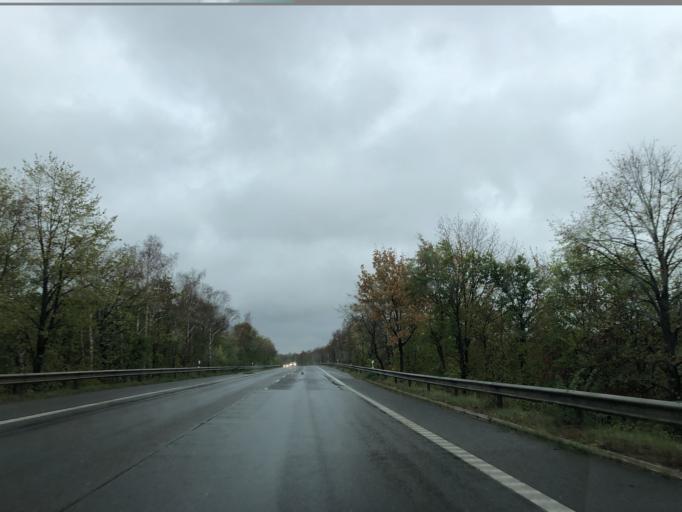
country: DE
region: North Rhine-Westphalia
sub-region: Regierungsbezirk Dusseldorf
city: Grevenbroich
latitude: 51.0451
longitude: 6.5661
